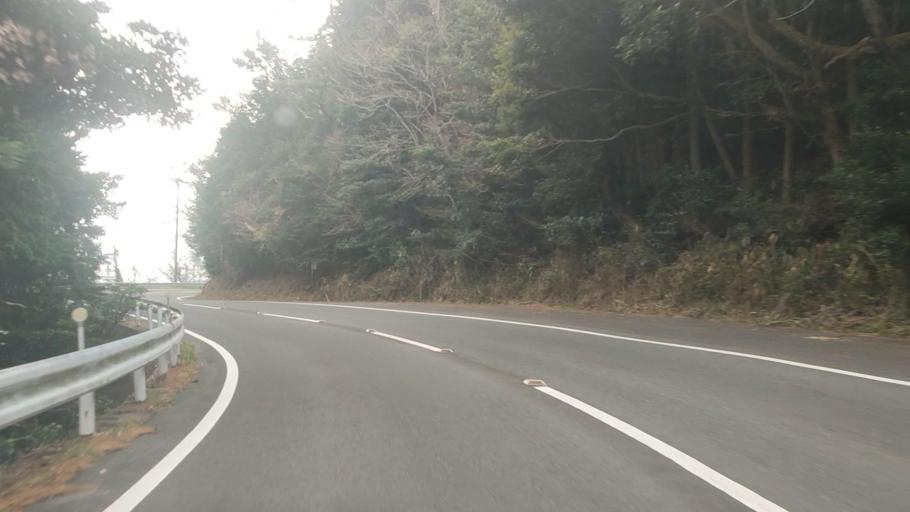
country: JP
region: Nagasaki
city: Shimabara
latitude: 32.7195
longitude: 130.2468
